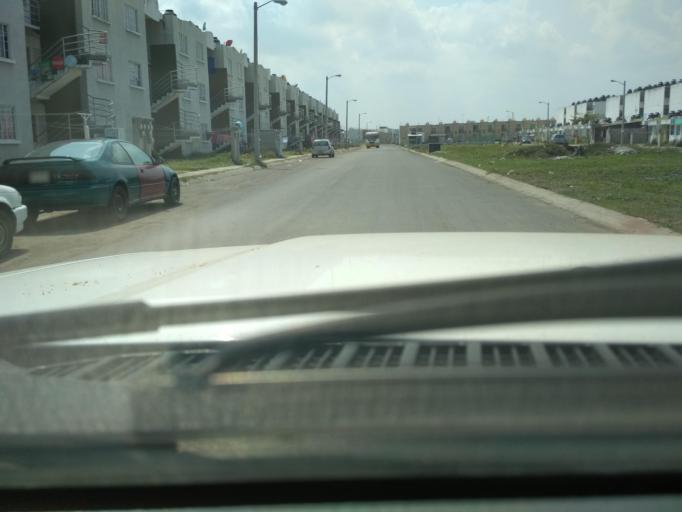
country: MX
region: Veracruz
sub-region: Veracruz
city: Lomas de Rio Medio Cuatro
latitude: 19.1875
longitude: -96.2062
